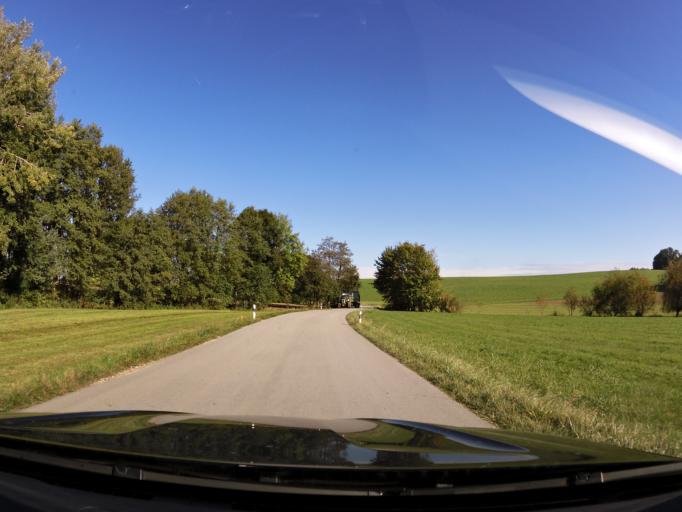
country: DE
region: Bavaria
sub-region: Lower Bavaria
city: Vilsheim
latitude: 48.4384
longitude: 12.1324
